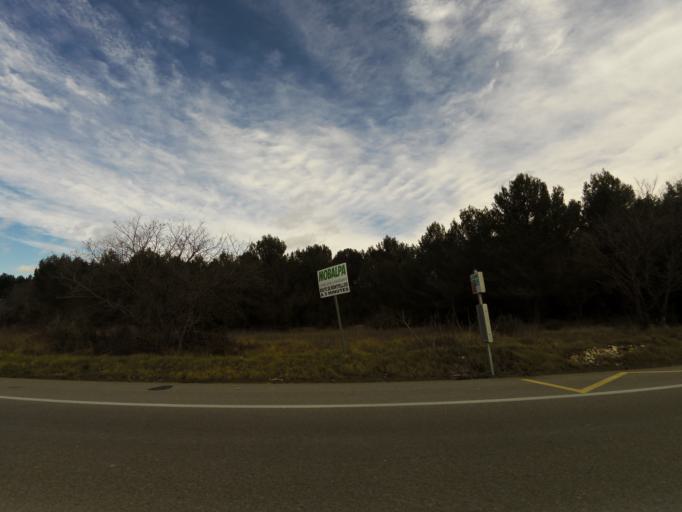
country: FR
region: Languedoc-Roussillon
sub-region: Departement du Gard
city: Caveirac
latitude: 43.8204
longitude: 4.2904
